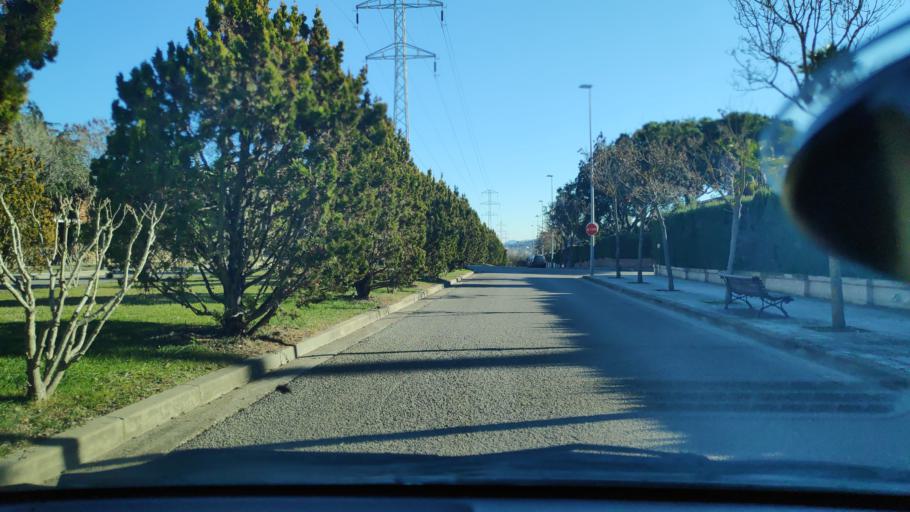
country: ES
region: Catalonia
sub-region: Provincia de Barcelona
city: Sant Quirze del Valles
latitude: 41.5388
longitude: 2.0645
